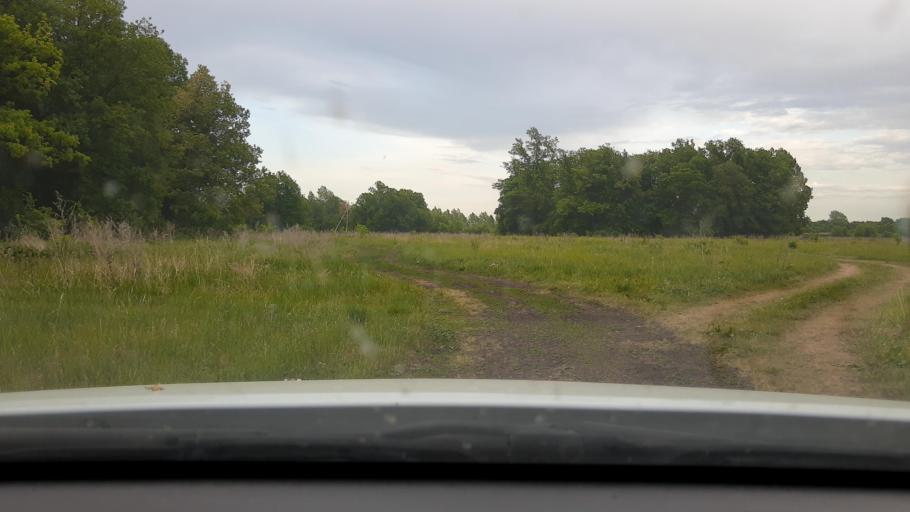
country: RU
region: Bashkortostan
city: Ufa
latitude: 54.6558
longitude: 55.8825
